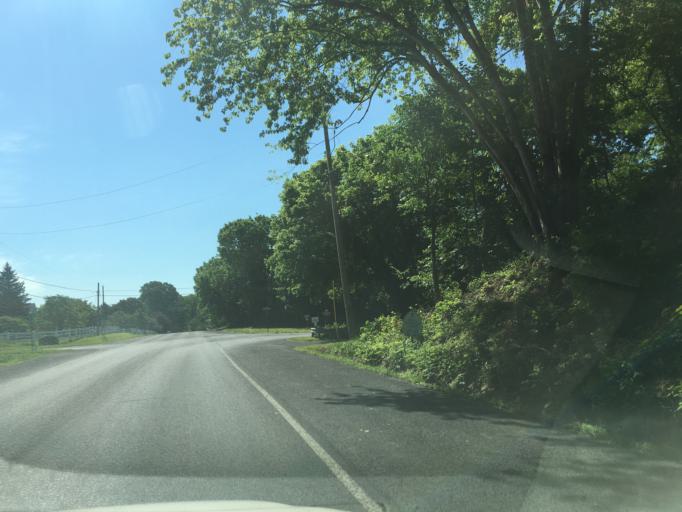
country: US
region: West Virginia
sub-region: Jefferson County
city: Bolivar
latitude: 39.3291
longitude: -77.6986
